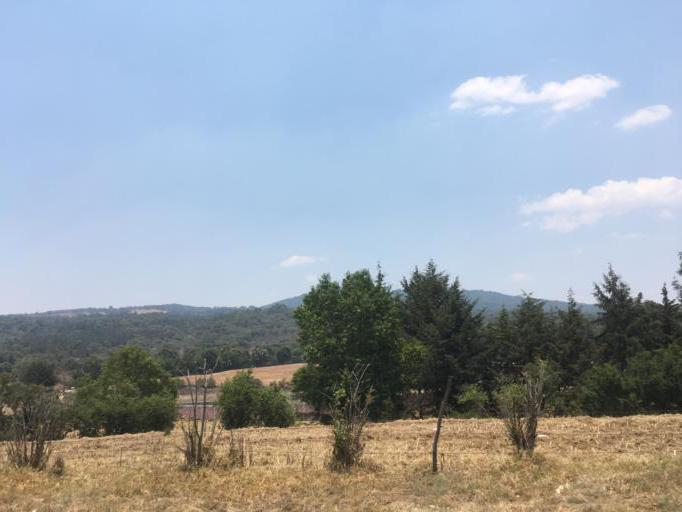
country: MX
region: Michoacan
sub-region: Morelia
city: Iratzio
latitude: 19.6329
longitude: -101.4691
